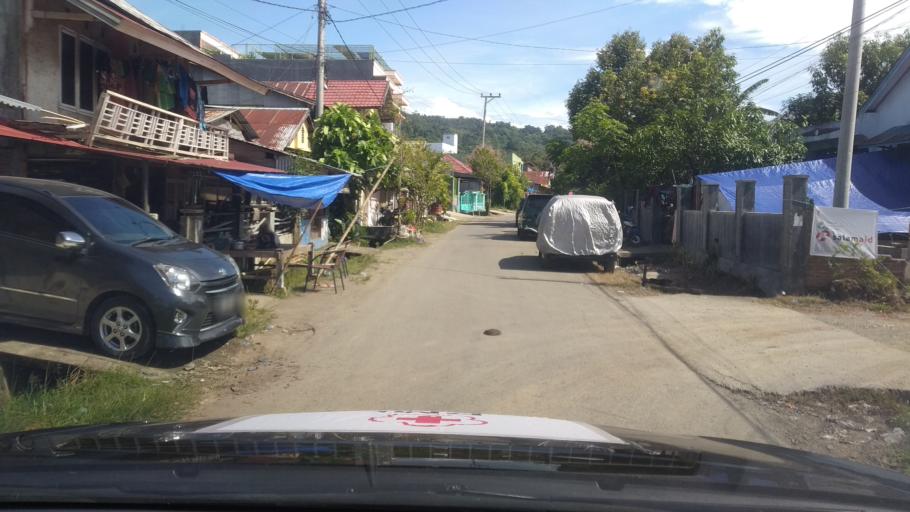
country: ID
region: Sulawesi Barat
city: Mamuju
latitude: -2.6891
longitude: 118.8790
